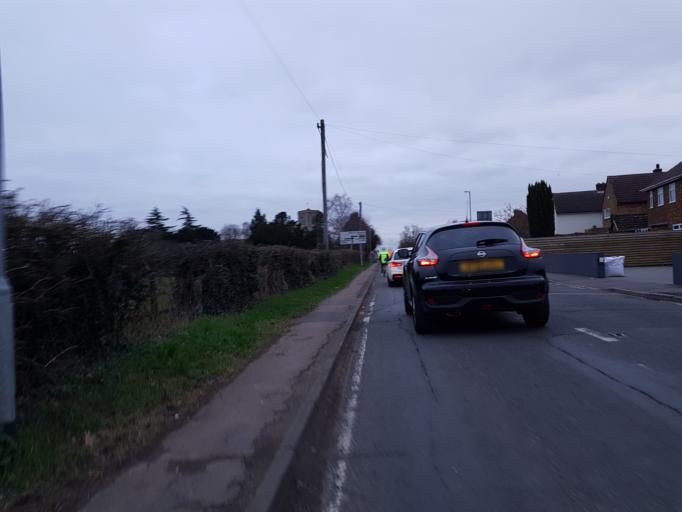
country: GB
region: England
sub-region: Cambridgeshire
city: Fulbourn
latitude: 52.2179
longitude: 0.2181
